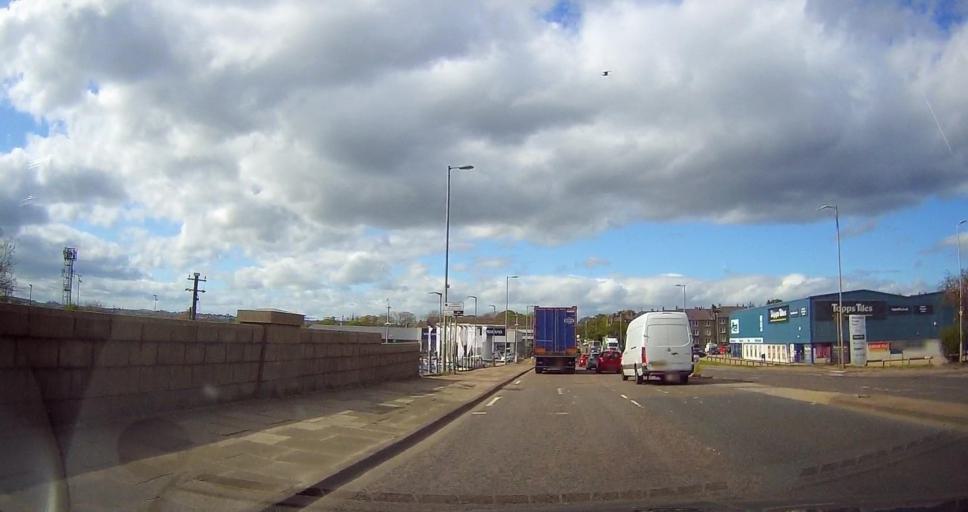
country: GB
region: Scotland
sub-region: Aberdeen City
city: Aberdeen
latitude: 57.1283
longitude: -2.0921
